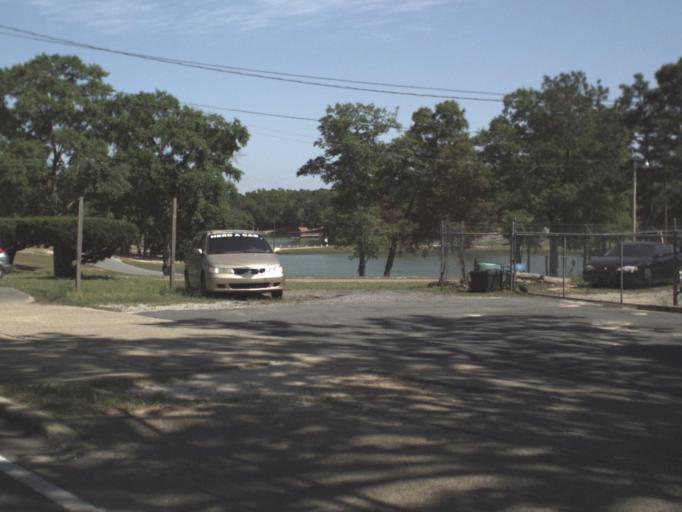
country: US
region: Florida
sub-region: Okaloosa County
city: Crestview
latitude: 30.7628
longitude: -86.5665
